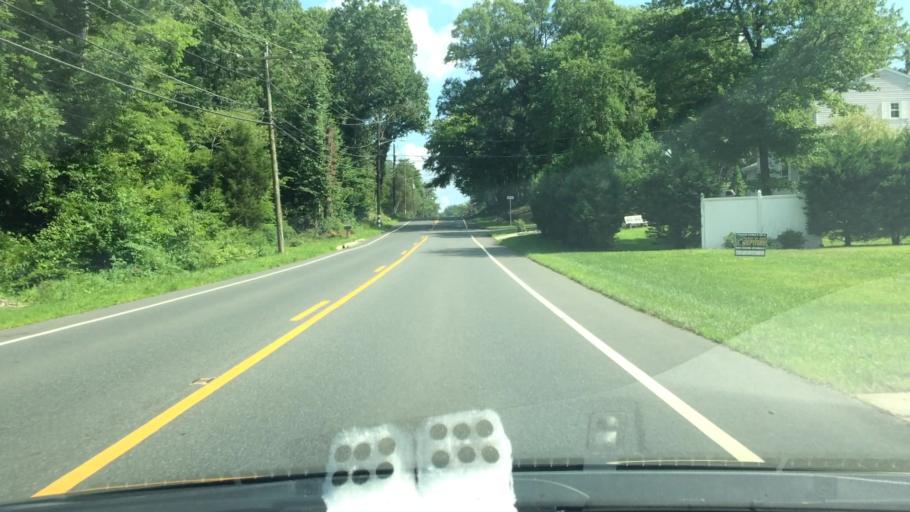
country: US
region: New Jersey
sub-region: Camden County
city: Blackwood
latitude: 39.8000
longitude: -75.0895
